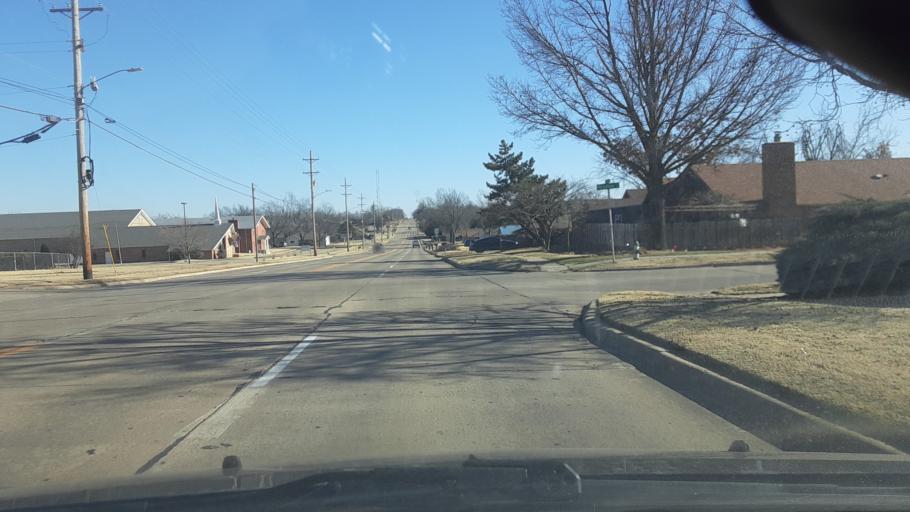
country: US
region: Oklahoma
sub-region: Kay County
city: Ponca City
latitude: 36.7385
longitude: -97.0621
